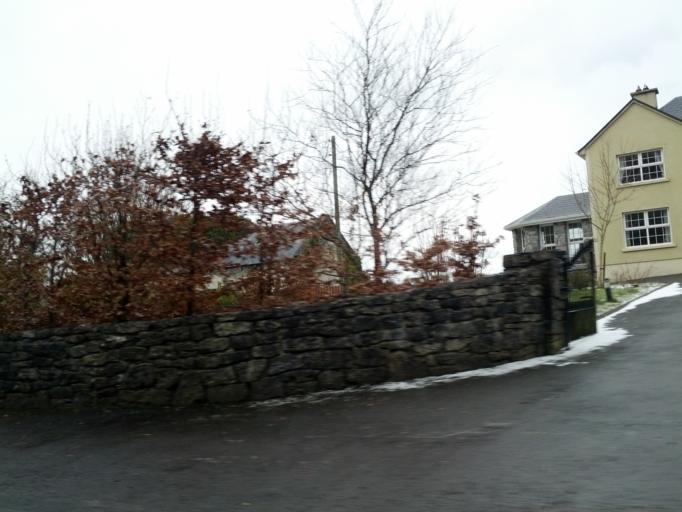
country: IE
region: Connaught
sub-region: County Galway
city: Oranmore
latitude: 53.2431
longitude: -8.8577
